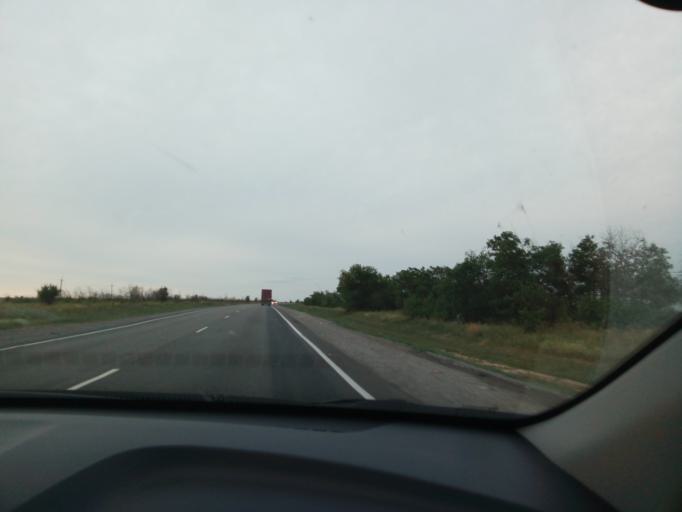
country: RU
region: Volgograd
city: Dubovka
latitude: 49.1445
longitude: 44.8300
